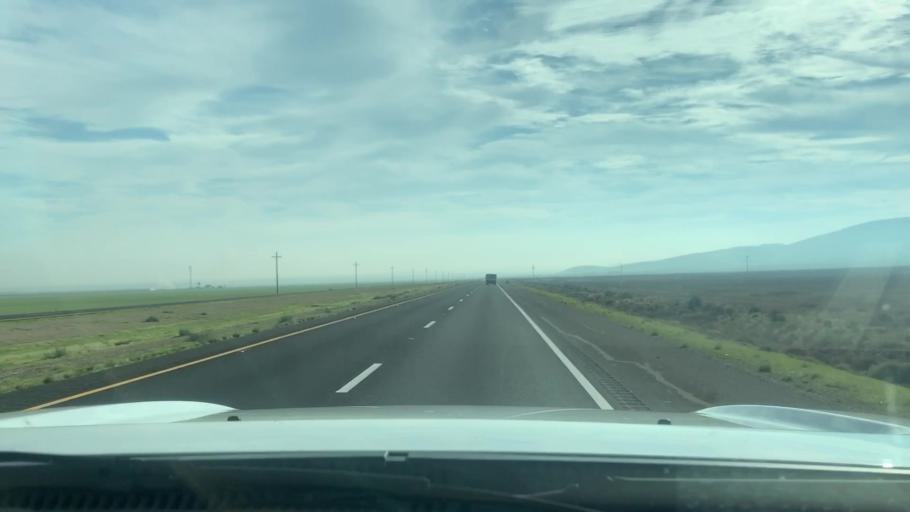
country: US
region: California
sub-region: San Luis Obispo County
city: Shandon
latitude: 35.6614
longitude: -120.0622
